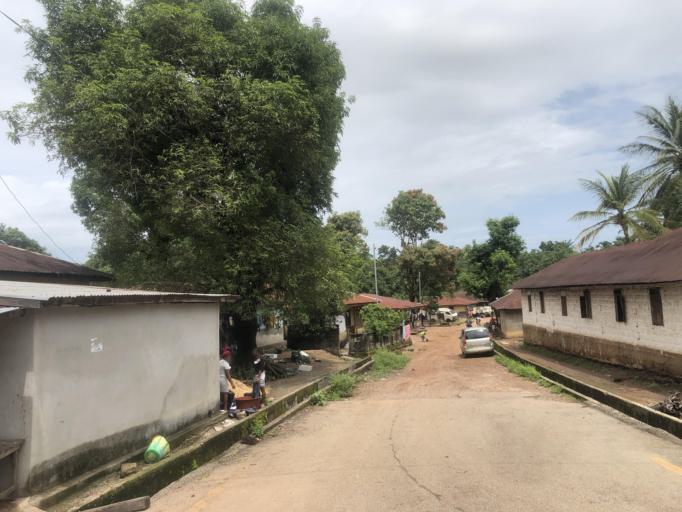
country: SL
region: Northern Province
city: Magburaka
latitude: 8.7184
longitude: -11.9382
